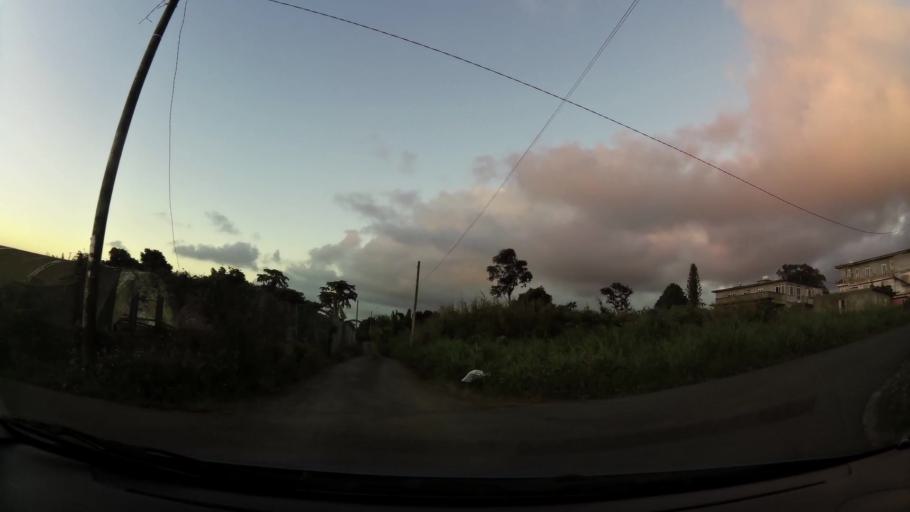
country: MU
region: Plaines Wilhems
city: Curepipe
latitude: -20.2991
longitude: 57.5273
